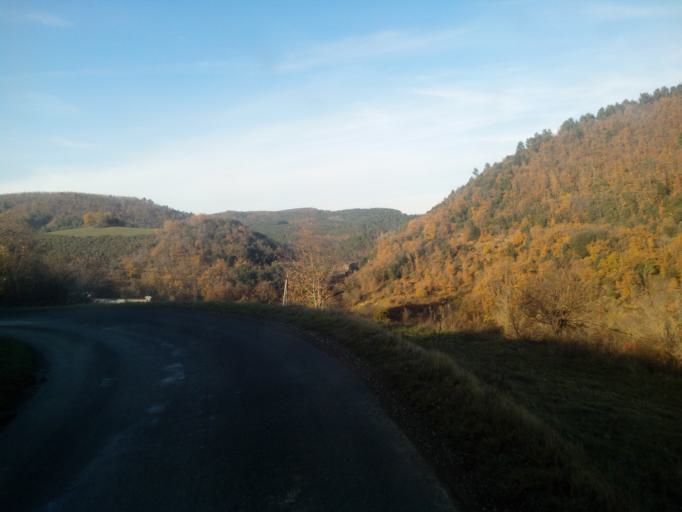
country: FR
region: Languedoc-Roussillon
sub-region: Departement de l'Aude
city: Couiza
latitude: 42.8895
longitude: 2.3170
